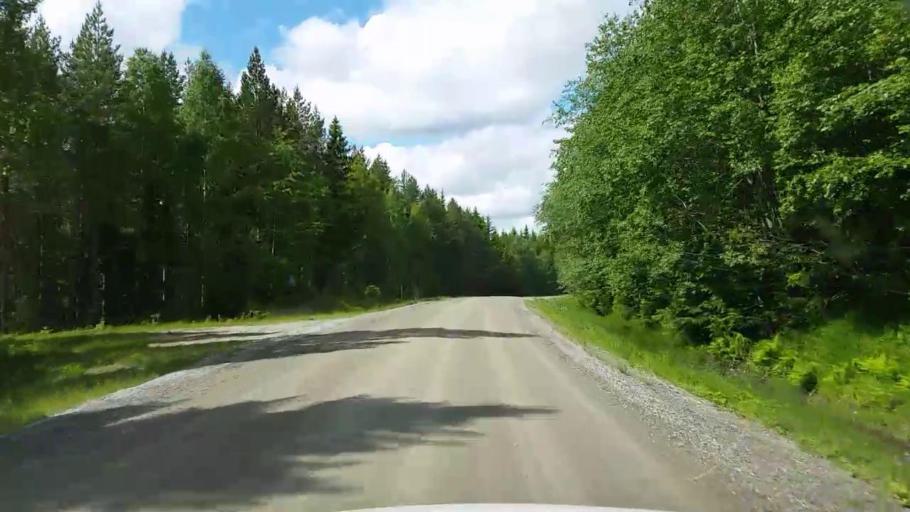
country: SE
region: Gaevleborg
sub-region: Bollnas Kommun
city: Vittsjo
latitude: 61.0452
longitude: 16.3392
